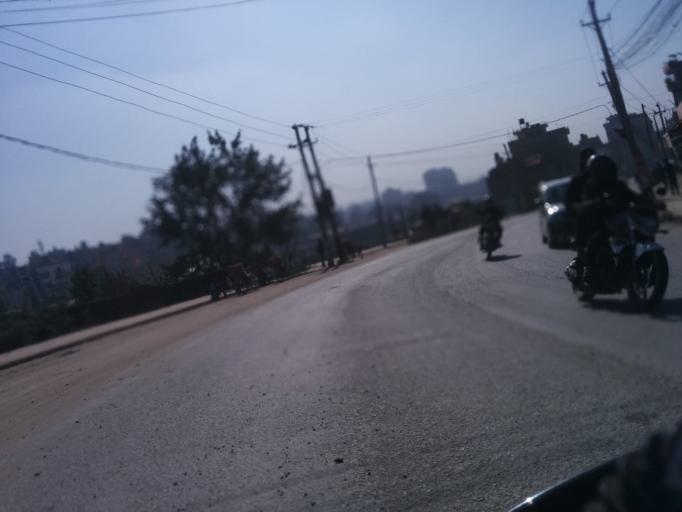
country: NP
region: Central Region
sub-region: Bagmati Zone
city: Patan
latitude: 27.6827
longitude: 85.2985
